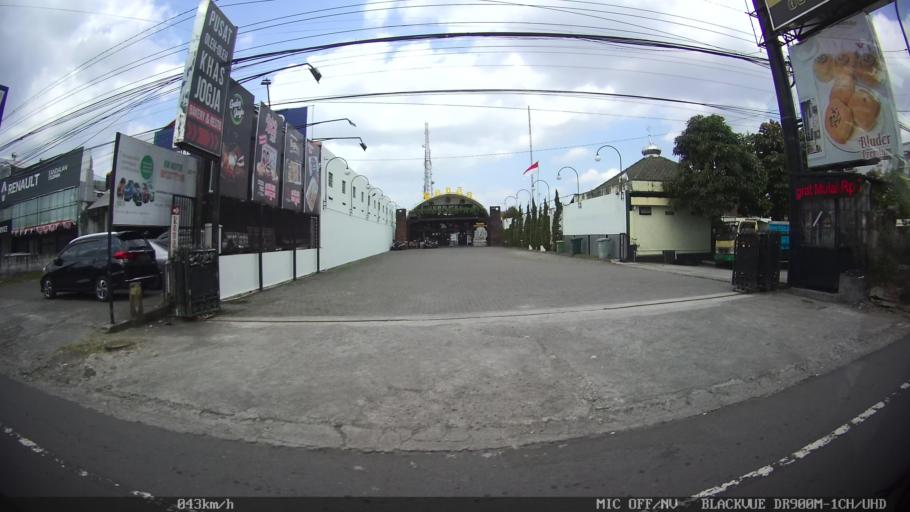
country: ID
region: Daerah Istimewa Yogyakarta
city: Yogyakarta
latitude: -7.7579
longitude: 110.3620
